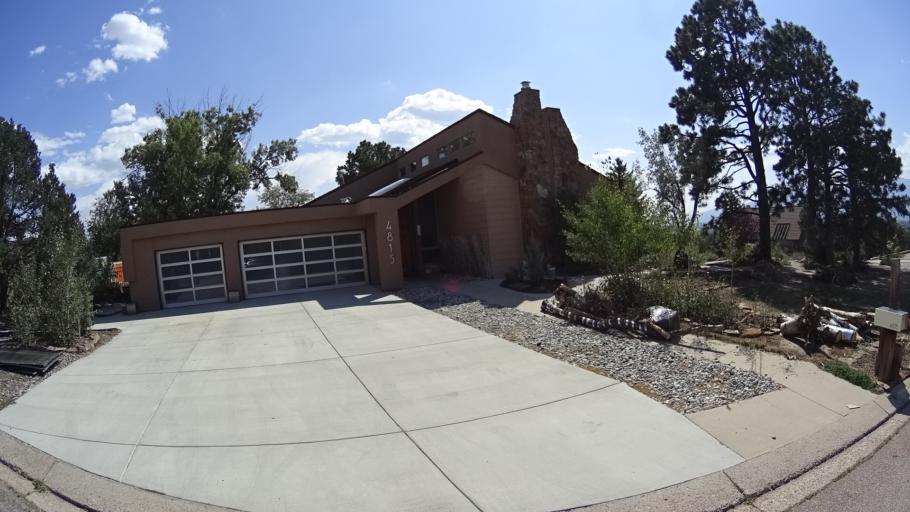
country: US
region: Colorado
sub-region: El Paso County
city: Cimarron Hills
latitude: 38.8700
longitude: -104.7399
